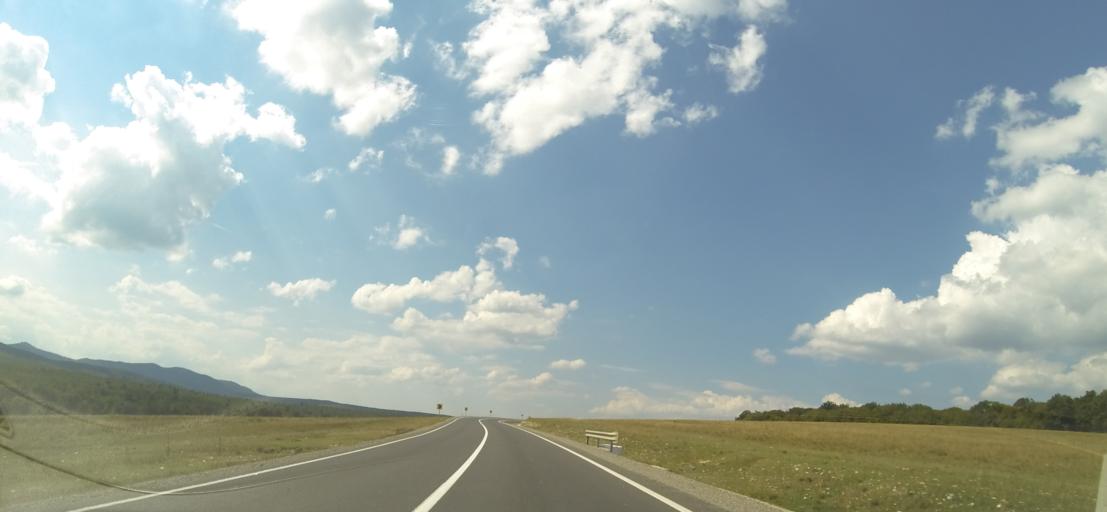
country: RO
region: Brasov
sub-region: Comuna Dumbravita
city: Dumbravita
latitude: 45.7488
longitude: 25.4089
